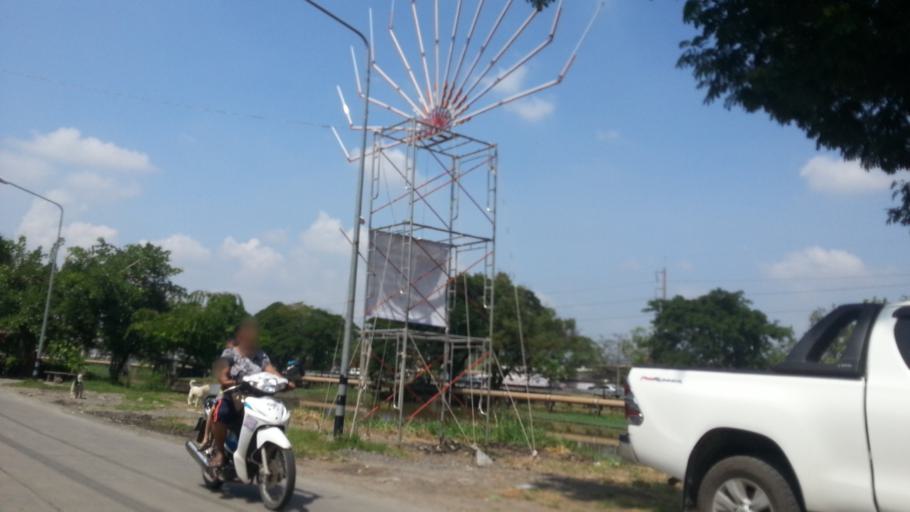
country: TH
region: Pathum Thani
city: Ban Rangsit
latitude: 14.0355
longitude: 100.7761
